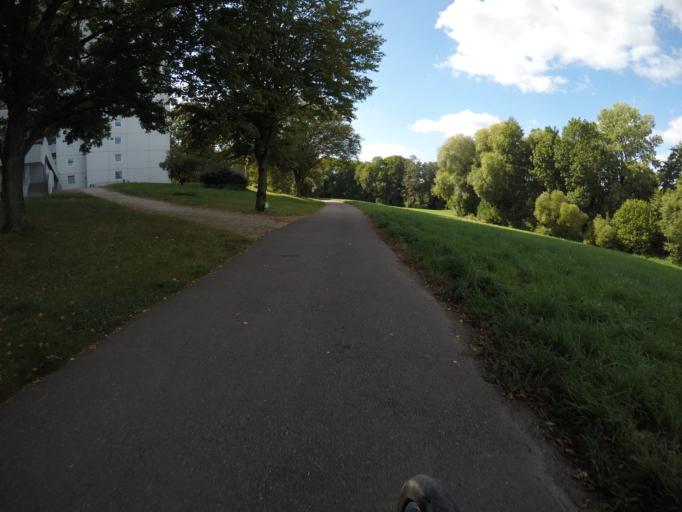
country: DE
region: Baden-Wuerttemberg
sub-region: Regierungsbezirk Stuttgart
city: Leinfelden-Echterdingen
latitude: 48.7152
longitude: 9.1499
